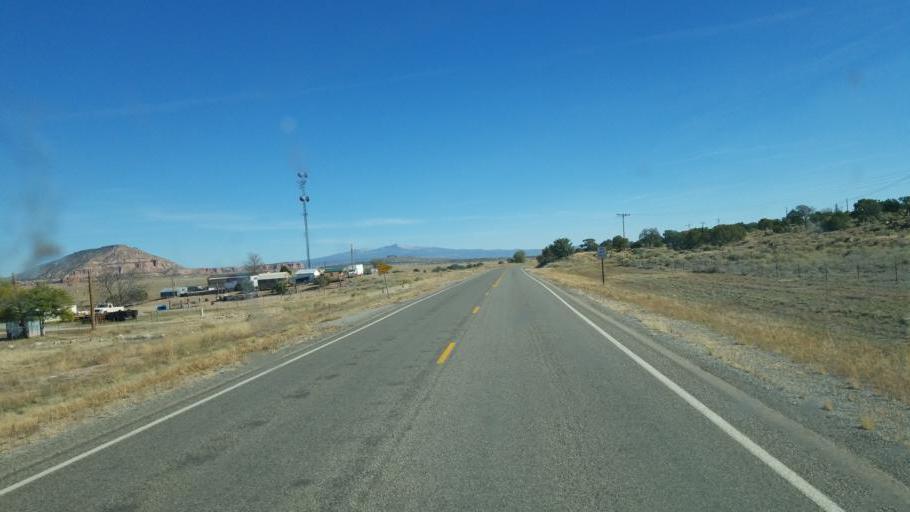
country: US
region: New Mexico
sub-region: McKinley County
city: Thoreau
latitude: 35.3553
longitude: -108.0215
